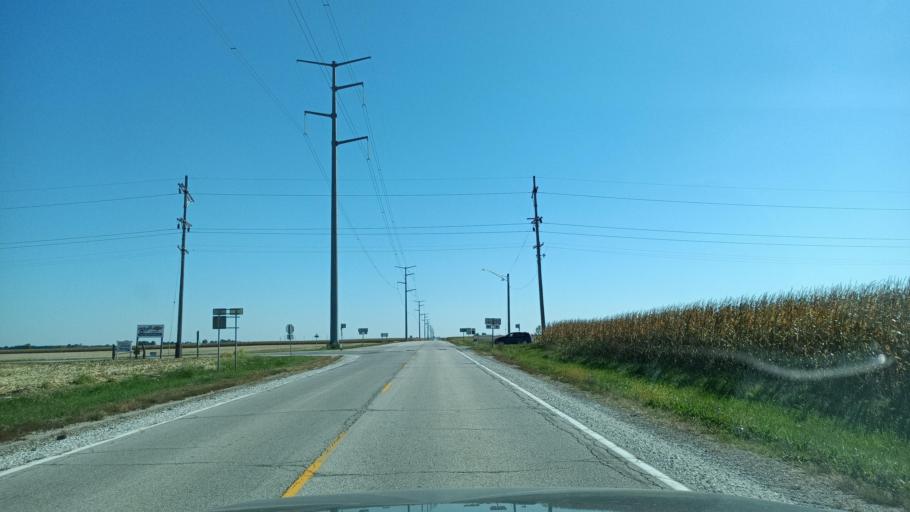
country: US
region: Illinois
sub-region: Peoria County
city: Elmwood
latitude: 40.9024
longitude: -90.0152
